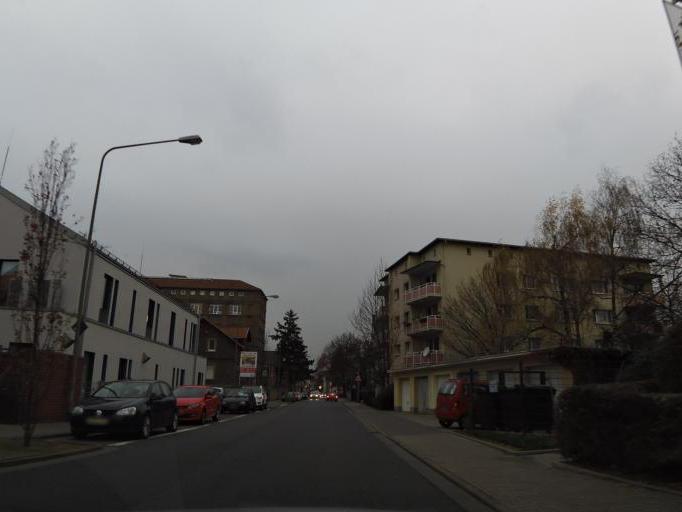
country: DE
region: Hesse
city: Niederrad
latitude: 50.0866
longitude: 8.5865
